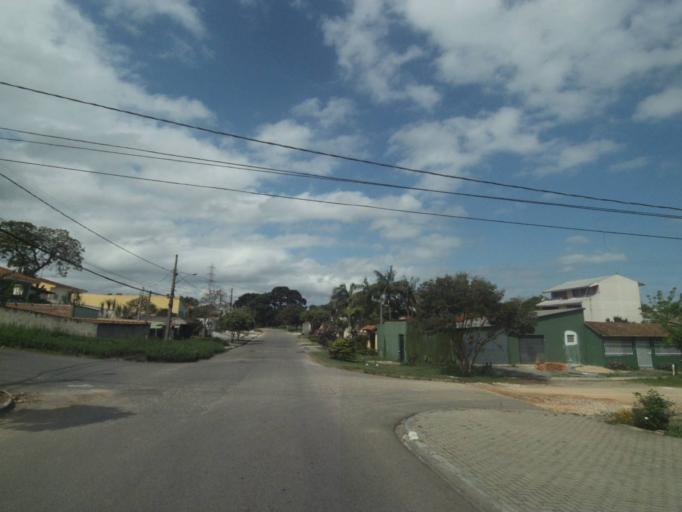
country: BR
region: Parana
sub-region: Pinhais
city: Pinhais
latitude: -25.4092
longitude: -49.1977
